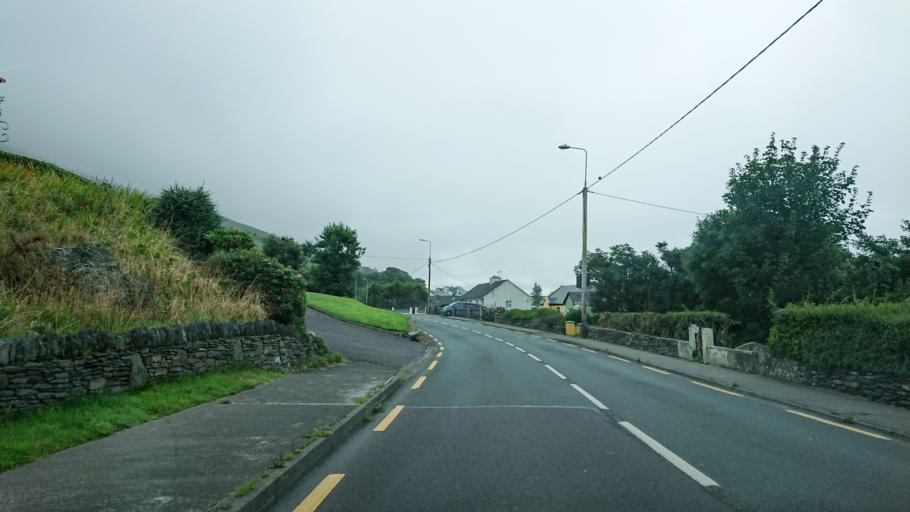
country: IE
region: Munster
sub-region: Ciarrai
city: Cahersiveen
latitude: 51.9501
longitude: -10.2161
